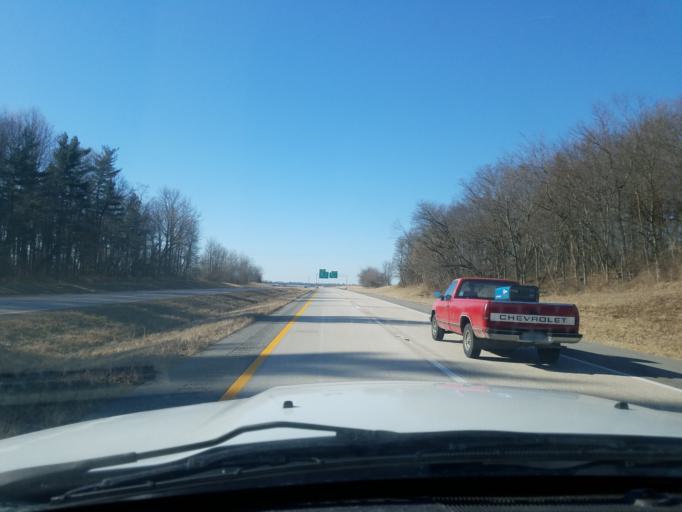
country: US
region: Kentucky
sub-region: Henderson County
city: Henderson
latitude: 37.8082
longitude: -87.5379
